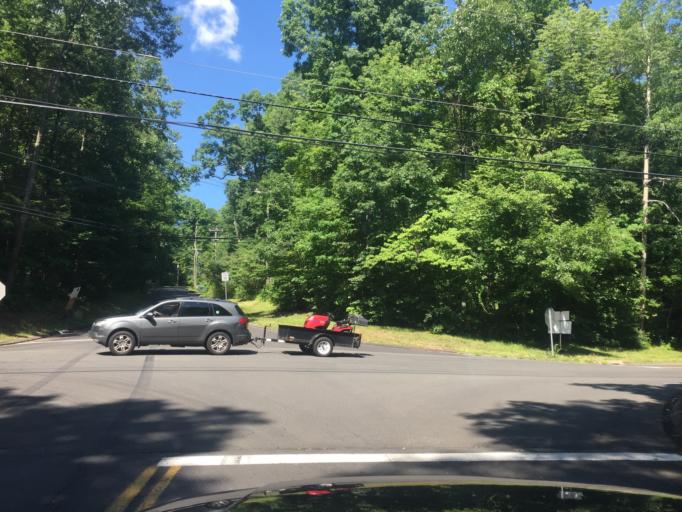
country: US
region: Connecticut
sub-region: Hartford County
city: Farmington
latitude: 41.7431
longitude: -72.8080
